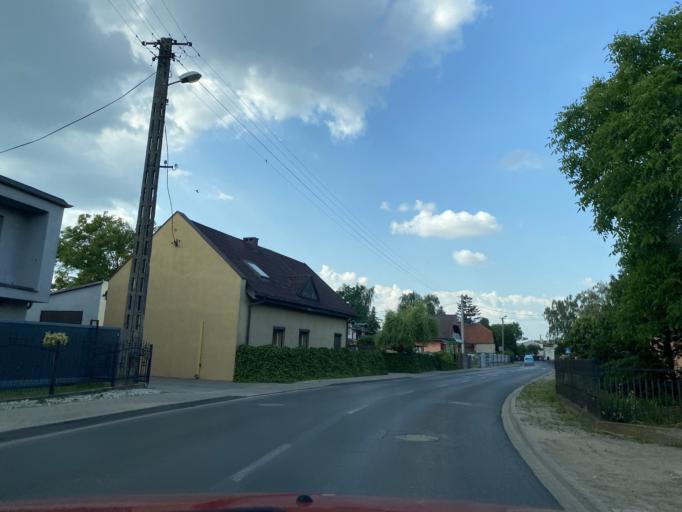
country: PL
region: Greater Poland Voivodeship
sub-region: Powiat poznanski
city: Dopiewo
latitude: 52.3686
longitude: 16.7359
